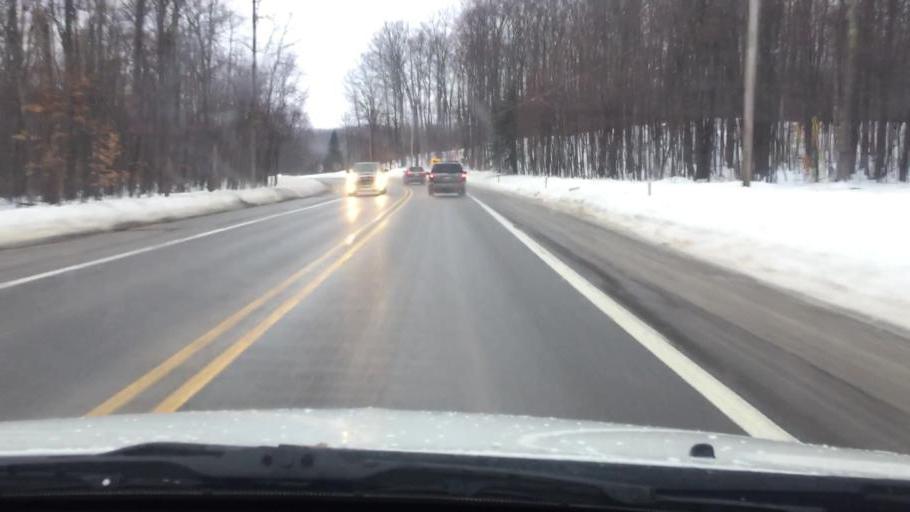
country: US
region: Michigan
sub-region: Charlevoix County
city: East Jordan
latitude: 45.2147
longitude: -85.1721
